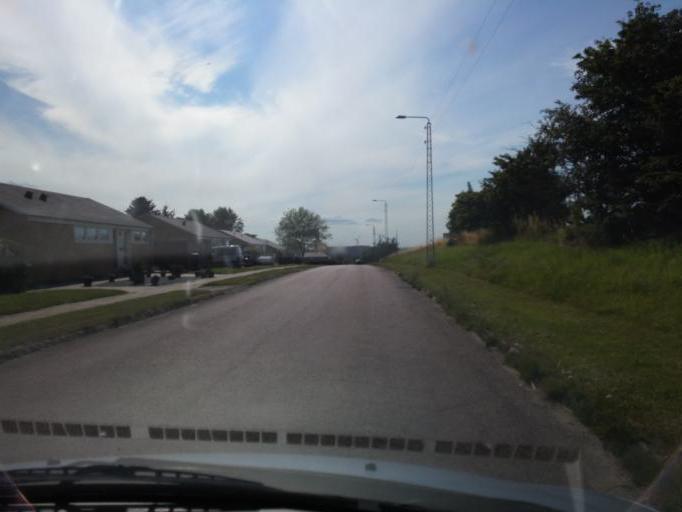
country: DK
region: South Denmark
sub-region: Kerteminde Kommune
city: Munkebo
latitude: 55.4653
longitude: 10.5579
